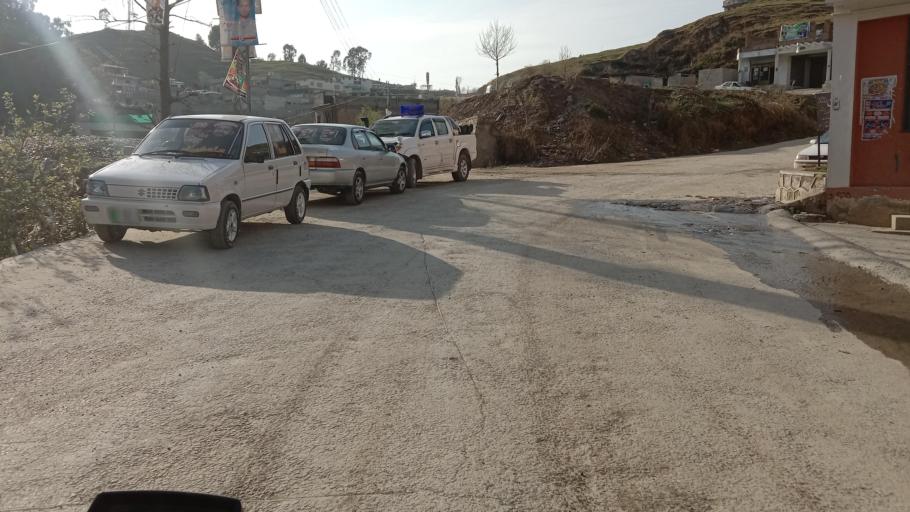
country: PK
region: Khyber Pakhtunkhwa
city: Abbottabad
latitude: 34.2031
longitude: 73.2221
